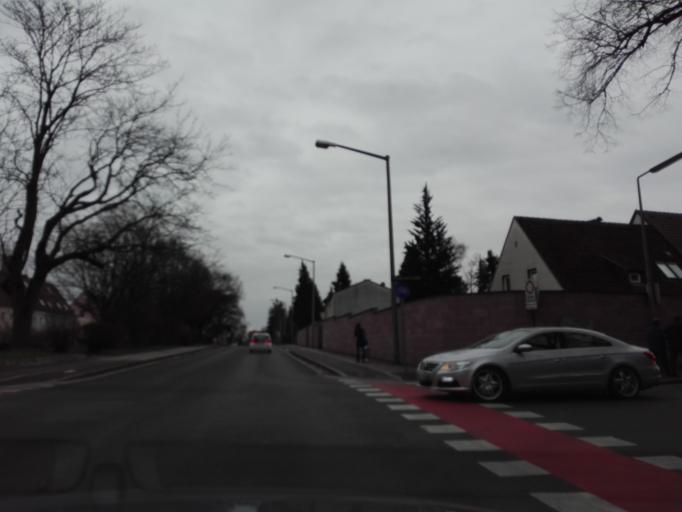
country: AT
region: Upper Austria
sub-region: Politischer Bezirk Linz-Land
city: Leonding
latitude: 48.2754
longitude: 14.2790
